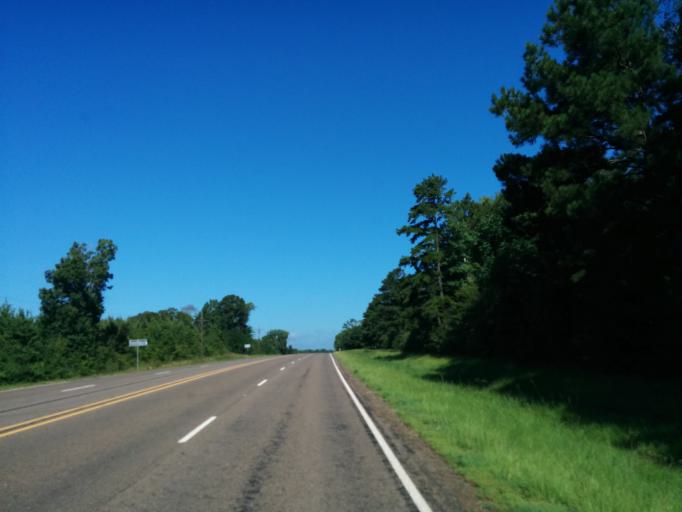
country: US
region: Texas
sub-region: Sabine County
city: Milam
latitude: 31.4313
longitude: -93.8256
